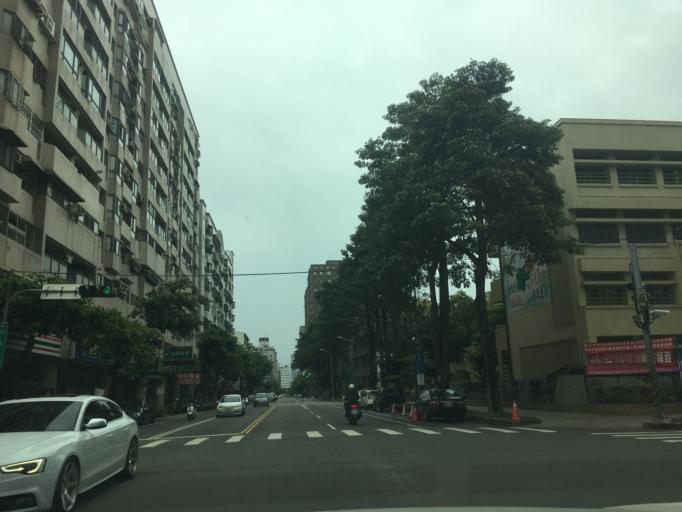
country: TW
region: Taiwan
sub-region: Taichung City
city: Taichung
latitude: 24.1693
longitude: 120.6600
